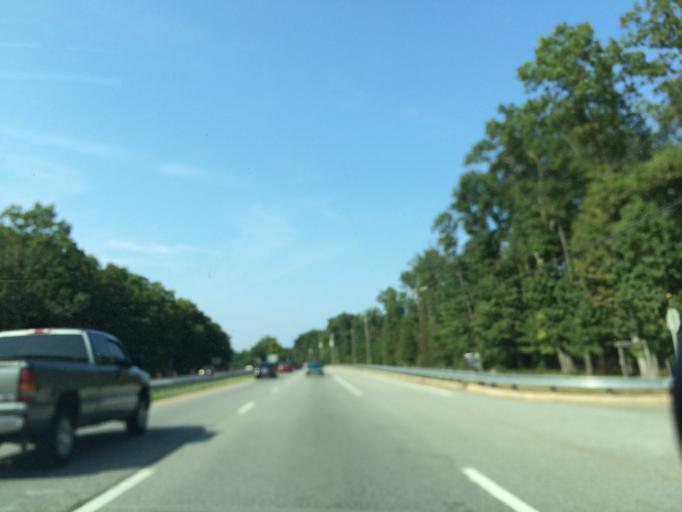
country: US
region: Maryland
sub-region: Charles County
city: La Plata
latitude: 38.5725
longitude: -76.9750
